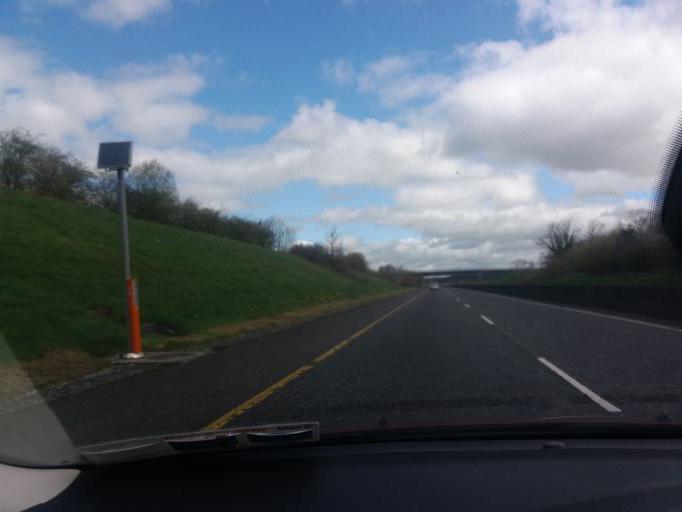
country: IE
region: Munster
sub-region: County Cork
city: Rathcormac
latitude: 52.0954
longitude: -8.2874
